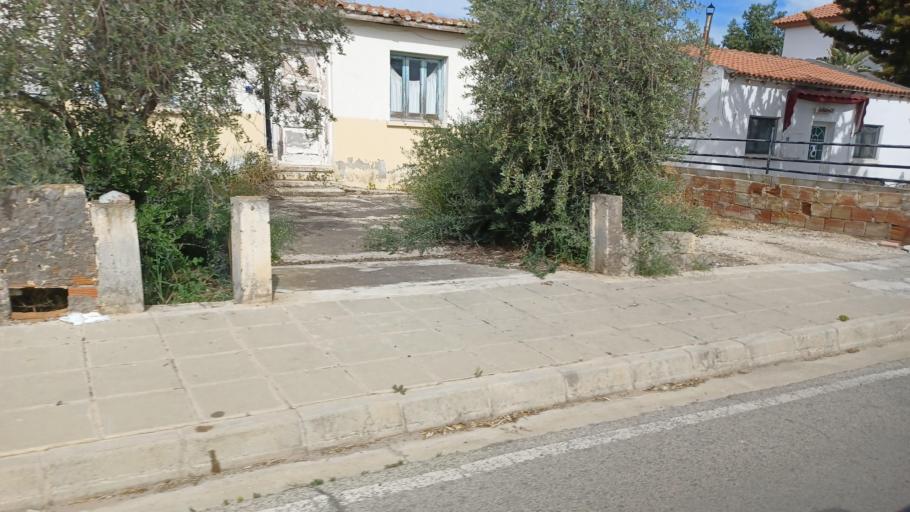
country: CY
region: Lefkosia
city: Kokkinotrimithia
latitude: 35.1583
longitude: 33.2053
